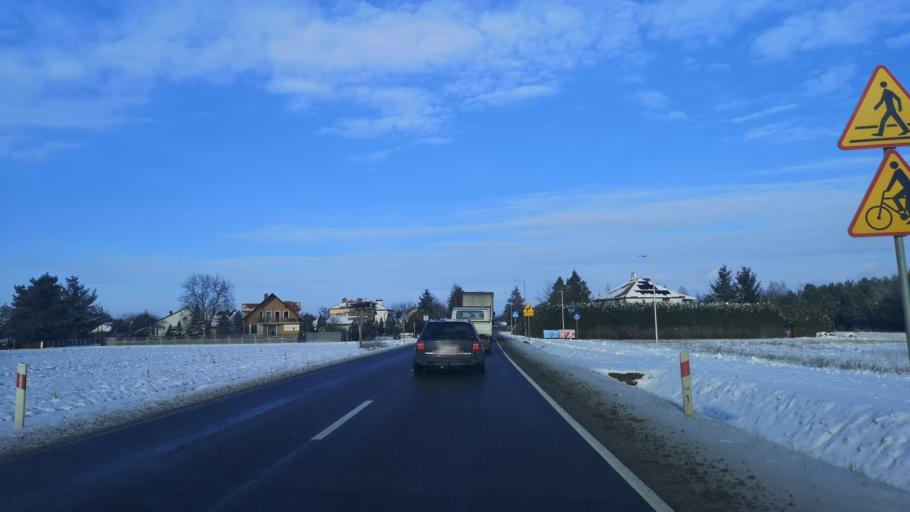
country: PL
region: Subcarpathian Voivodeship
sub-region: Powiat przeworski
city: Tryncza
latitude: 50.1332
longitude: 22.5367
